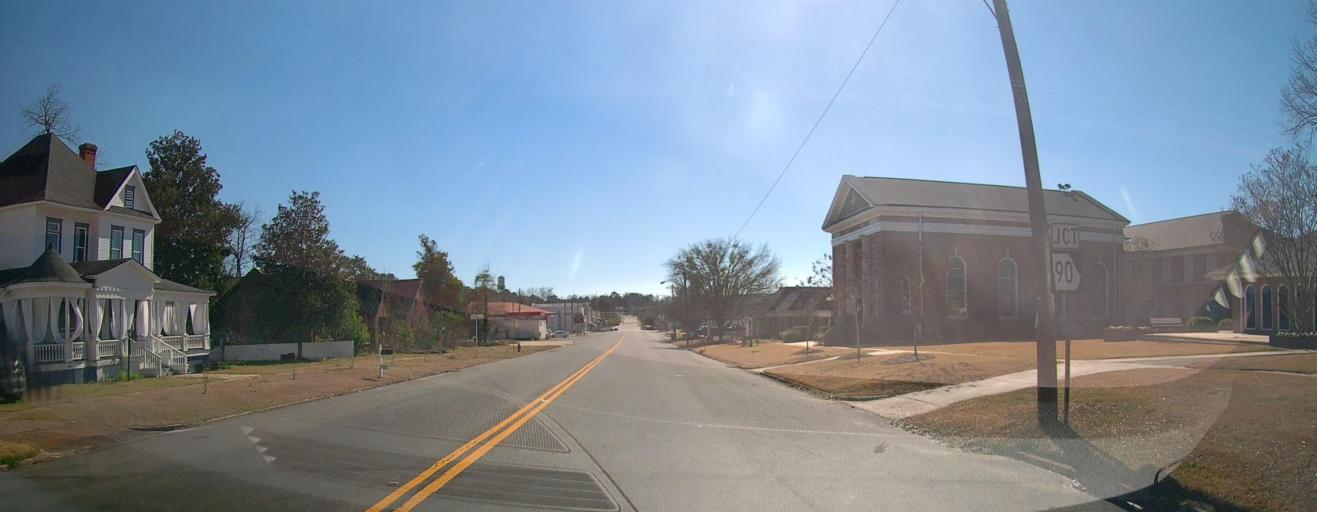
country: US
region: Georgia
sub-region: Macon County
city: Montezuma
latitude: 32.3026
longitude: -84.0291
